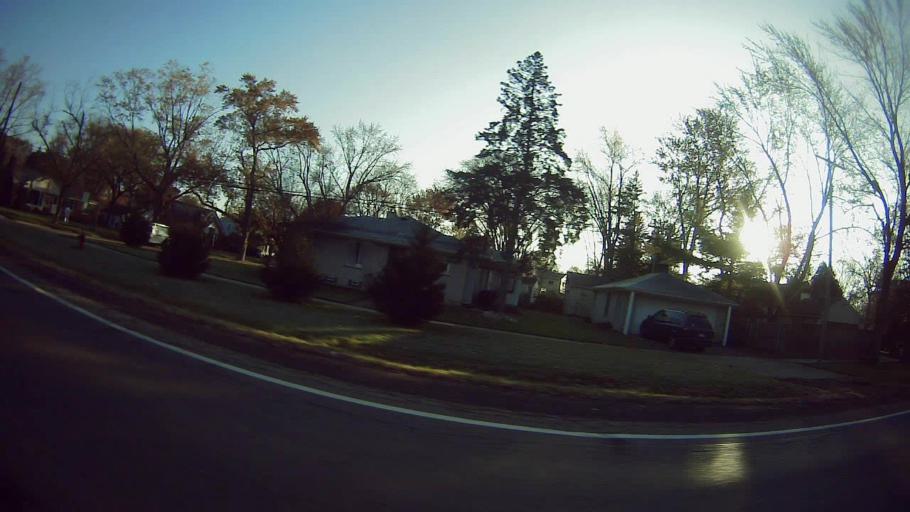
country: US
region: Michigan
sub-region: Oakland County
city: Beverly Hills
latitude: 42.5259
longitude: -83.2041
